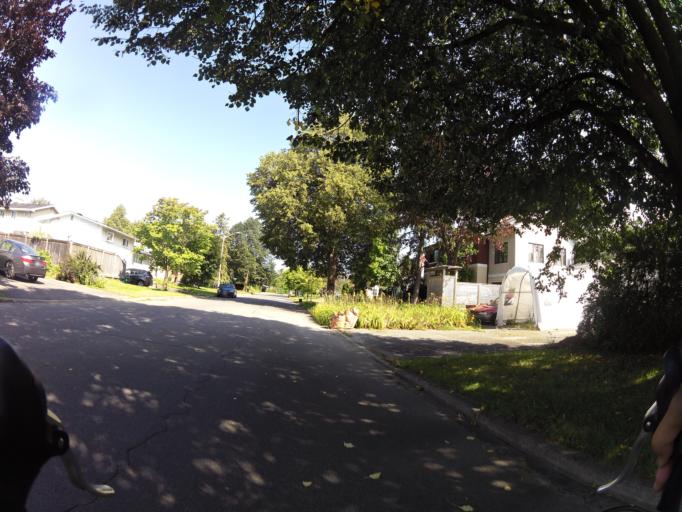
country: CA
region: Ontario
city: Ottawa
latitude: 45.3771
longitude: -75.6622
